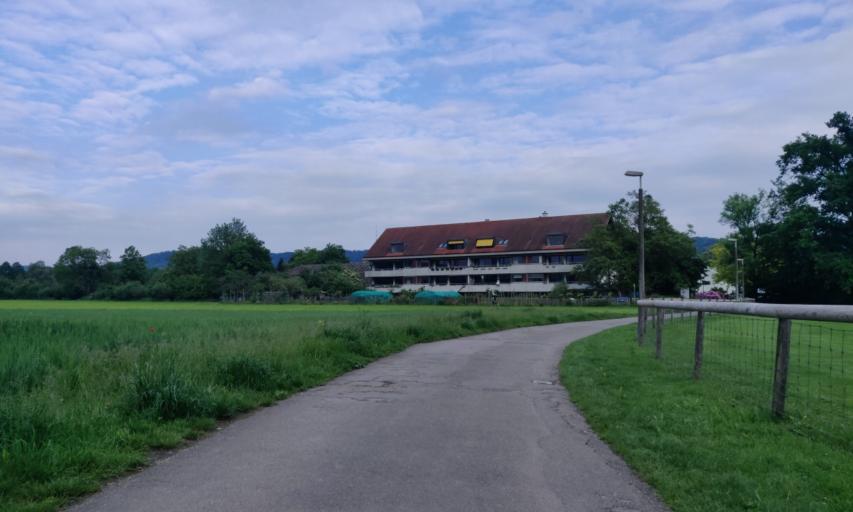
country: CH
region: Basel-City
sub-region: Basel-Stadt
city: Riehen
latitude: 47.5823
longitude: 7.6376
